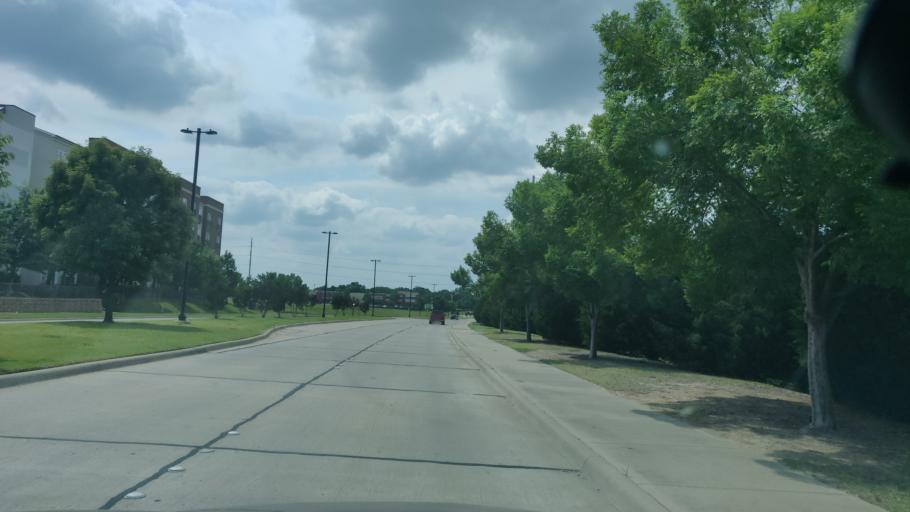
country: US
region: Texas
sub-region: Dallas County
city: Sachse
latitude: 32.9557
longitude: -96.6115
